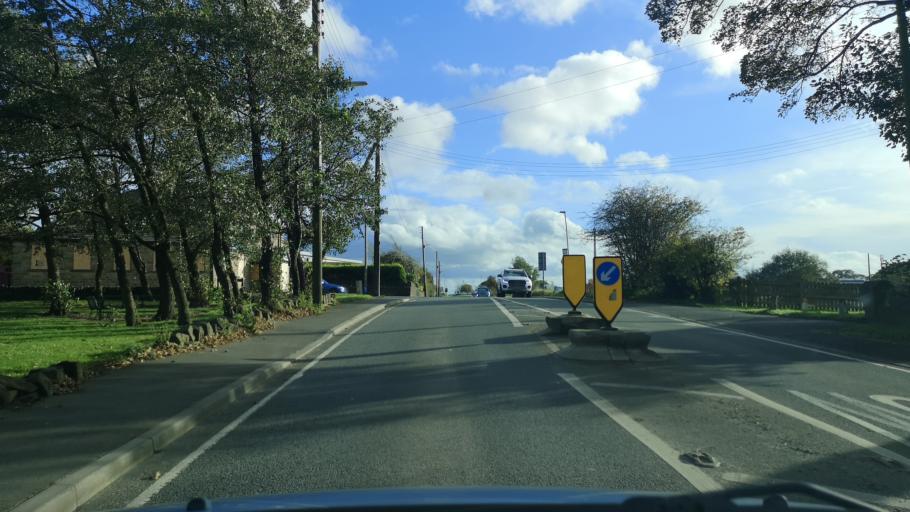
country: GB
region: England
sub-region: Kirklees
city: Shelley
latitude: 53.6392
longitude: -1.6680
